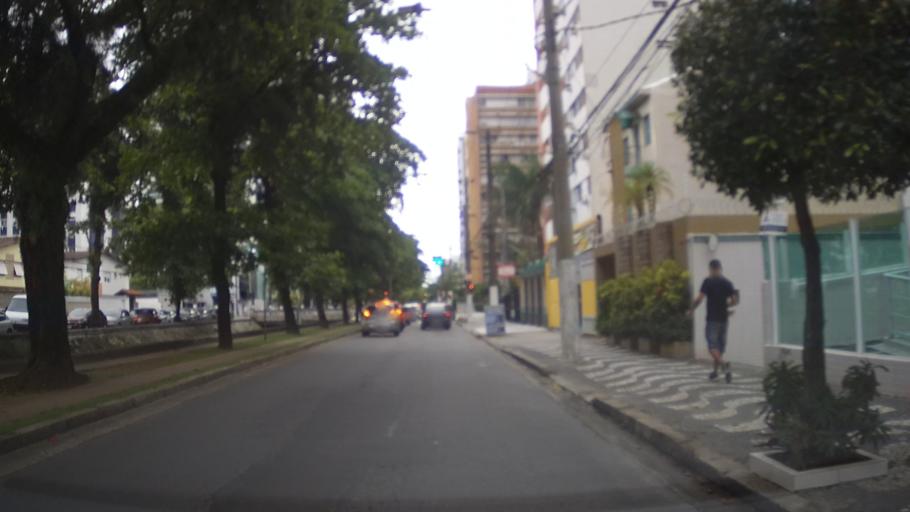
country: BR
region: Sao Paulo
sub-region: Santos
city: Santos
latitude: -23.9832
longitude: -46.3082
